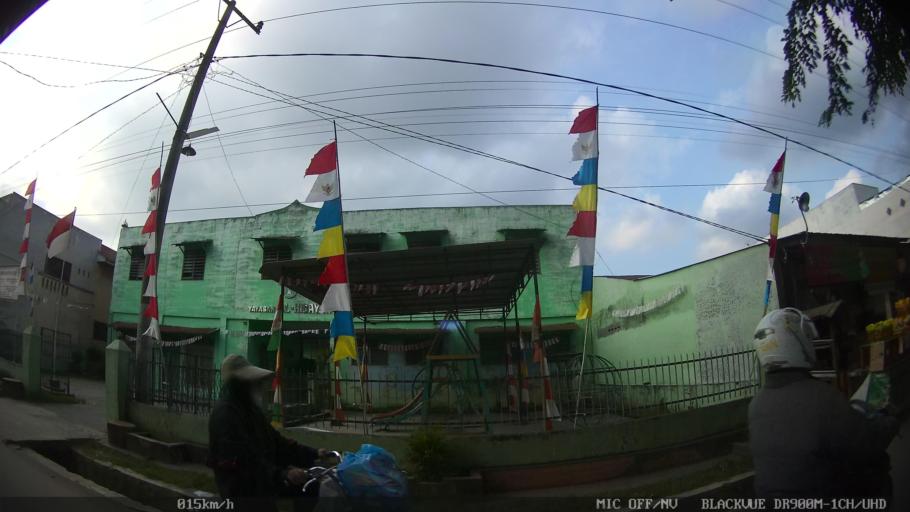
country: ID
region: North Sumatra
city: Medan
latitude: 3.5814
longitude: 98.7386
